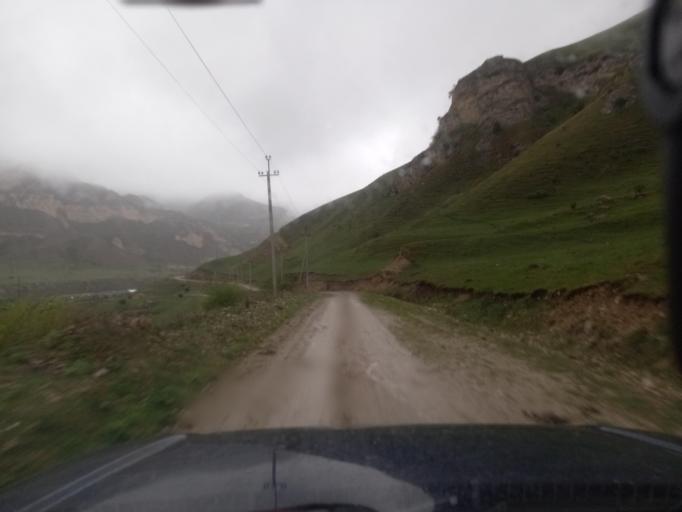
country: RU
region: Kabardino-Balkariya
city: Zhankhoteko
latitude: 43.5055
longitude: 43.1551
